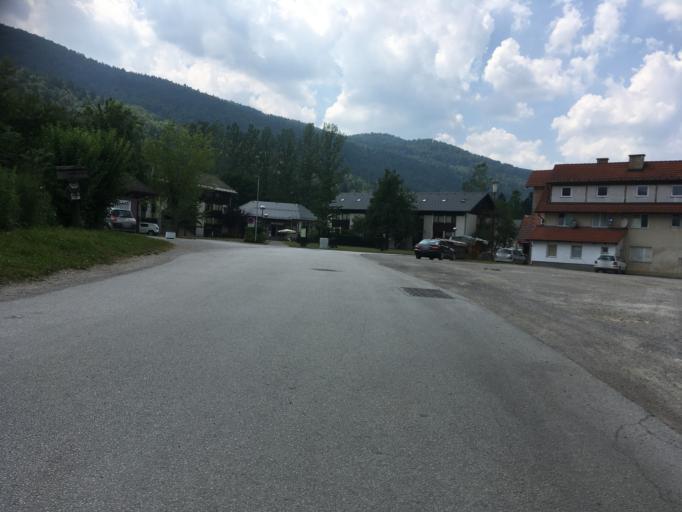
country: SI
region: Kocevje
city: Kocevje
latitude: 45.6415
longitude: 14.8477
